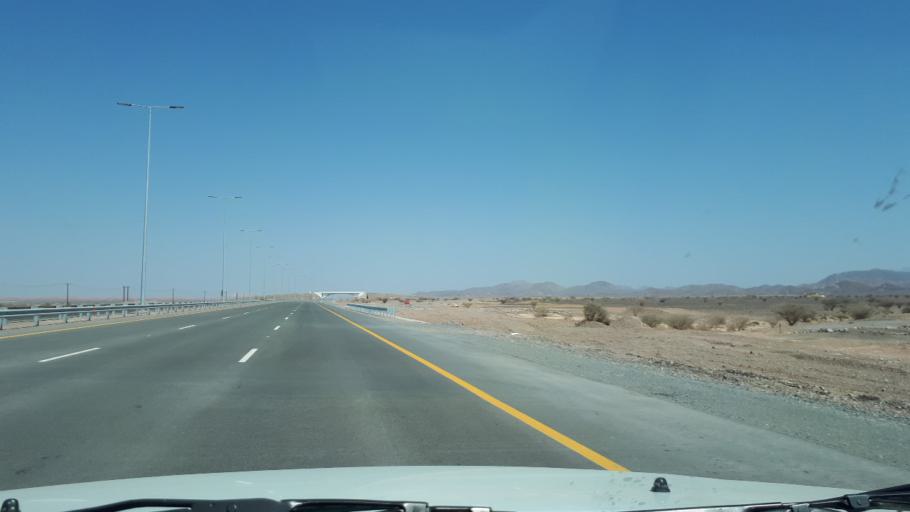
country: OM
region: Ash Sharqiyah
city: Badiyah
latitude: 22.4290
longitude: 59.0363
